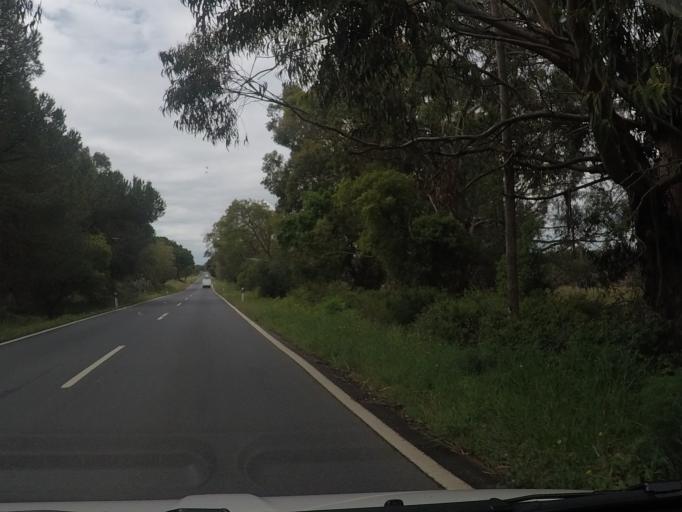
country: PT
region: Setubal
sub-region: Sines
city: Porto Covo
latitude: 37.8825
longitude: -8.7487
